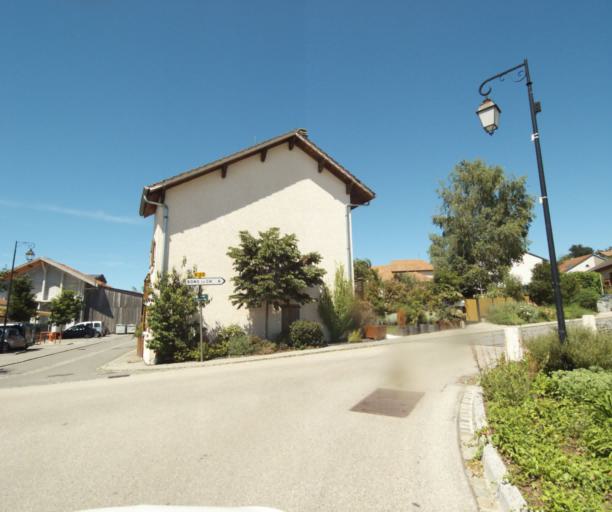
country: FR
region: Rhone-Alpes
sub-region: Departement de la Haute-Savoie
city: Ballaison
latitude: 46.2987
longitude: 6.3276
